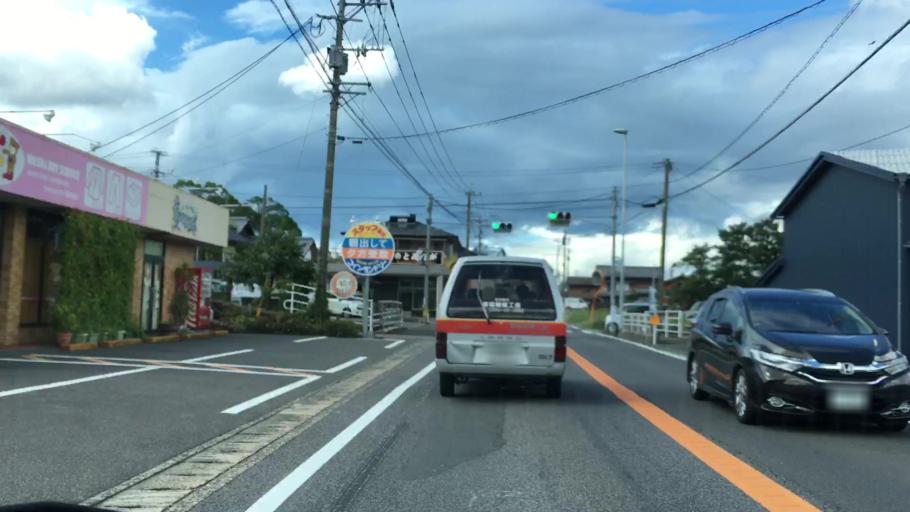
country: JP
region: Saga Prefecture
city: Imaricho-ko
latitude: 33.2036
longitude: 129.8502
